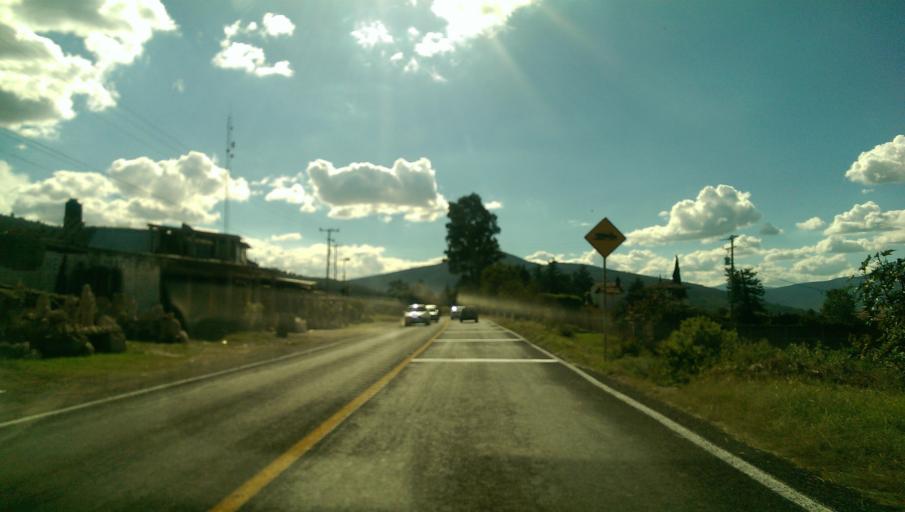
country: MX
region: Michoacan
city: Tzintzuntzan
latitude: 19.6391
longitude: -101.5486
